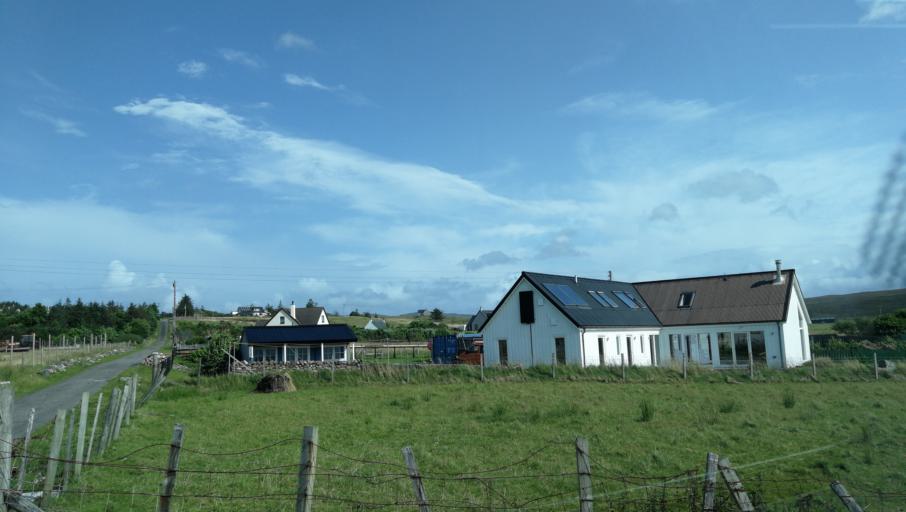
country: GB
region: Scotland
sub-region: Highland
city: Portree
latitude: 57.7424
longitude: -5.7774
